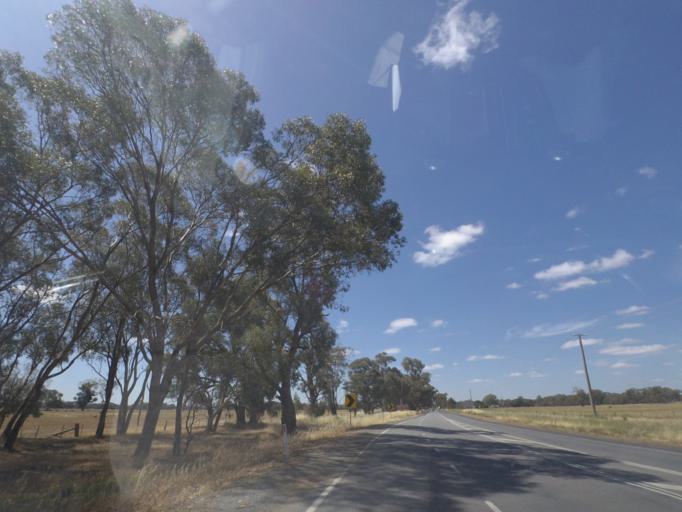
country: AU
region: Victoria
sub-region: Wangaratta
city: Wangaratta
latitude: -36.4057
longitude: 146.2730
